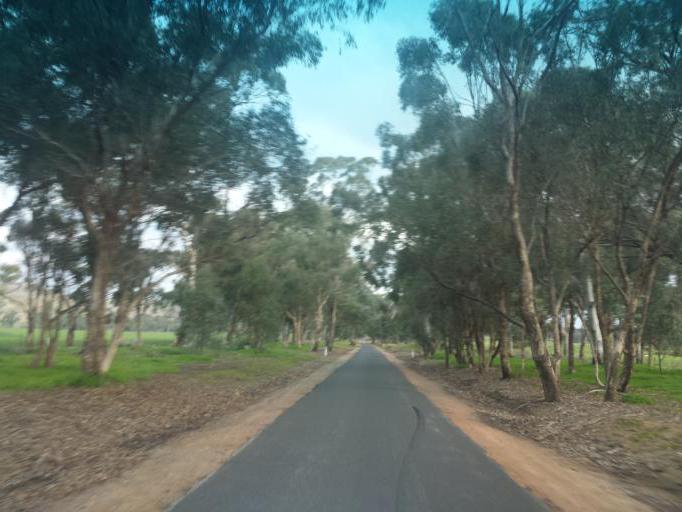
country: AU
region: Victoria
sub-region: Murrindindi
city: Kinglake West
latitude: -36.9242
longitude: 145.2242
